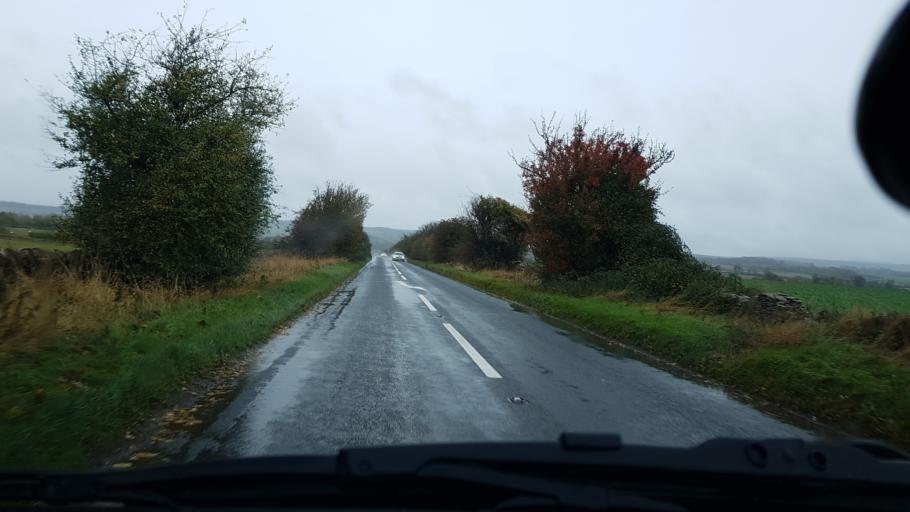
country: GB
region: England
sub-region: Gloucestershire
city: Stow on the Wold
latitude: 51.9438
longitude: -1.7758
